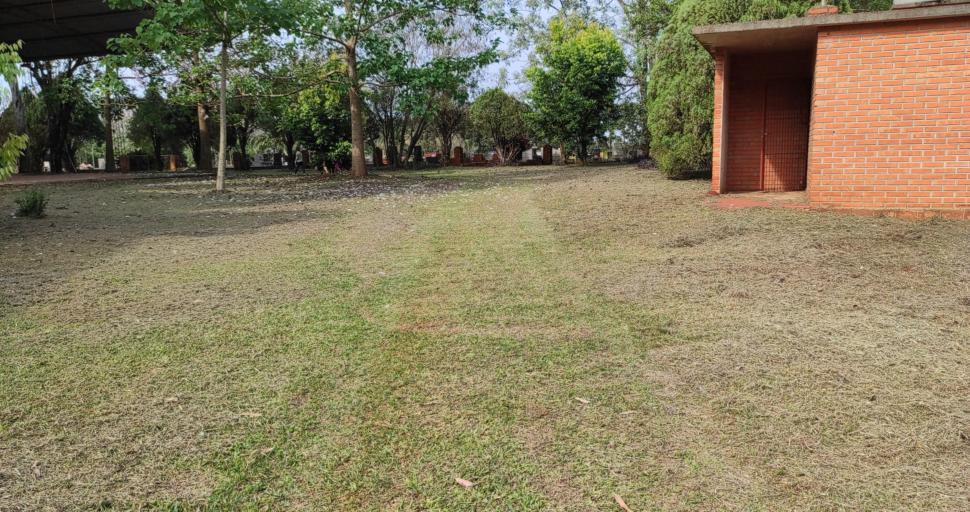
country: AR
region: Misiones
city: Garuhape
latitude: -26.8670
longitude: -54.9944
